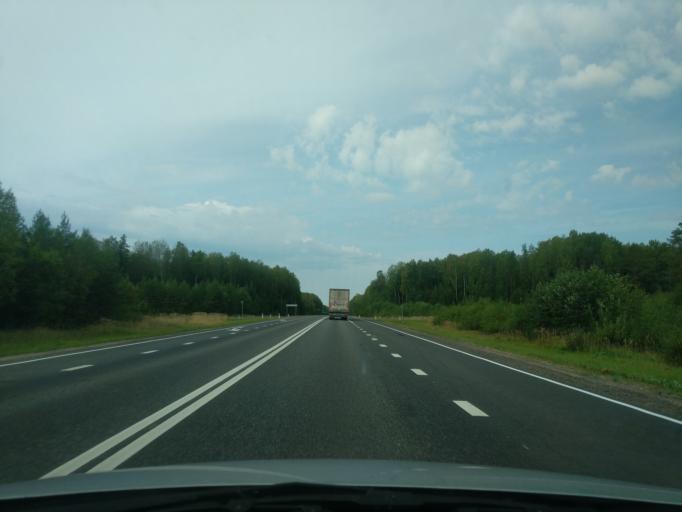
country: RU
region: Kirov
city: Leninskoye
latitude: 58.3189
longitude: 46.8783
